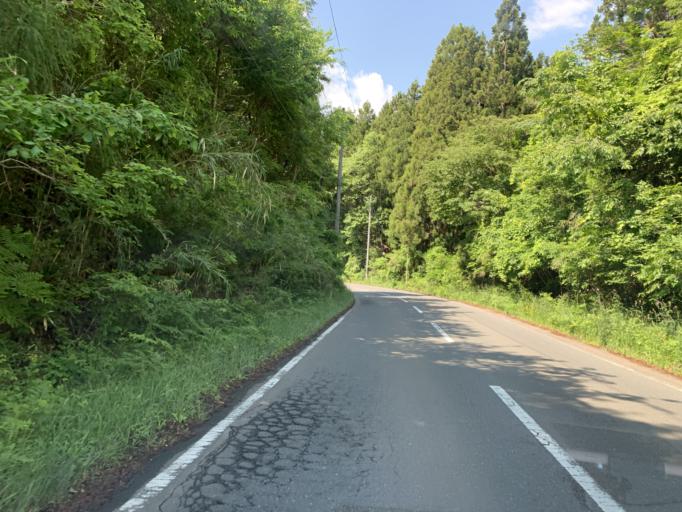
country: JP
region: Miyagi
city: Furukawa
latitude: 38.7130
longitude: 140.9426
